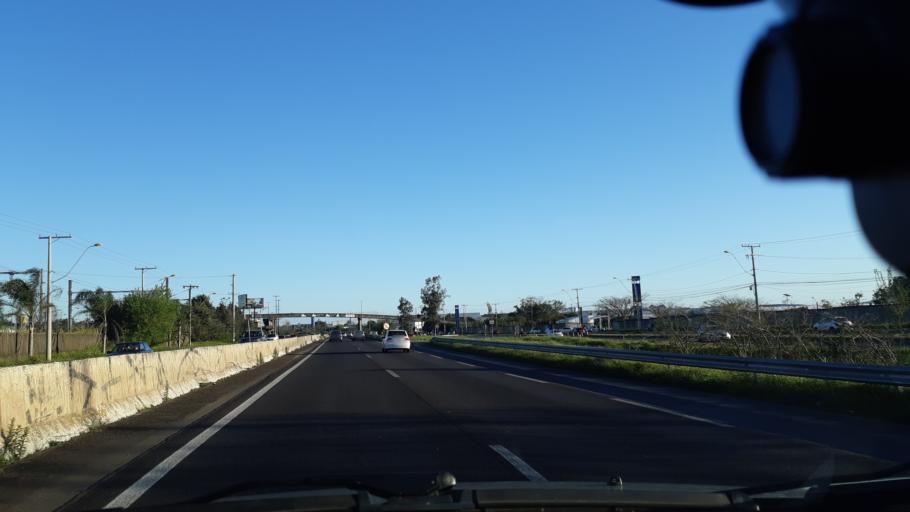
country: BR
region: Rio Grande do Sul
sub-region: Esteio
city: Esteio
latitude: -29.8568
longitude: -51.1805
